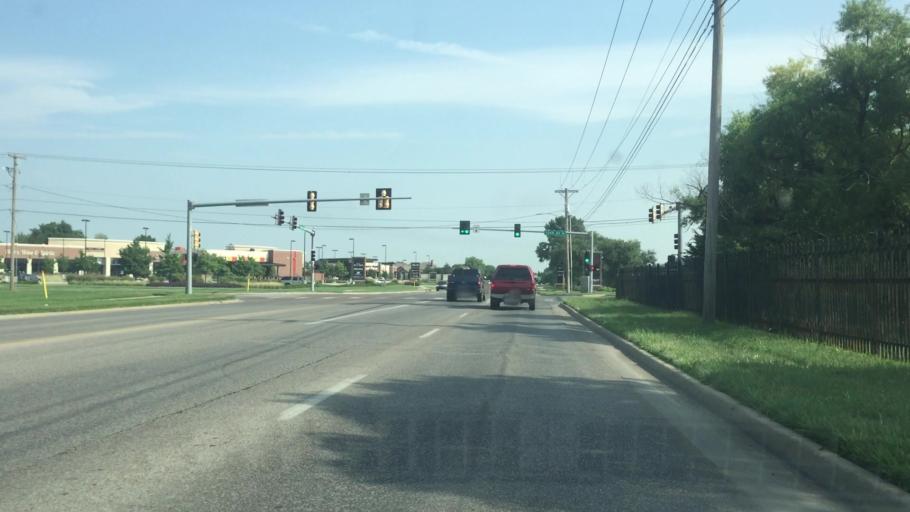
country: US
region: Kansas
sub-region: Sedgwick County
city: Bellaire
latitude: 37.7078
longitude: -97.2262
